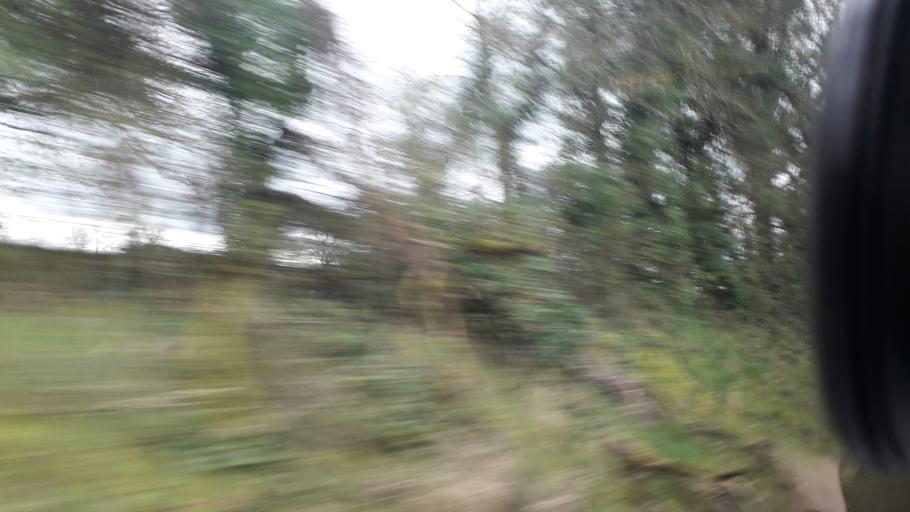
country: IE
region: Leinster
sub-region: An Longfort
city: Edgeworthstown
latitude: 53.6942
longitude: -7.6330
